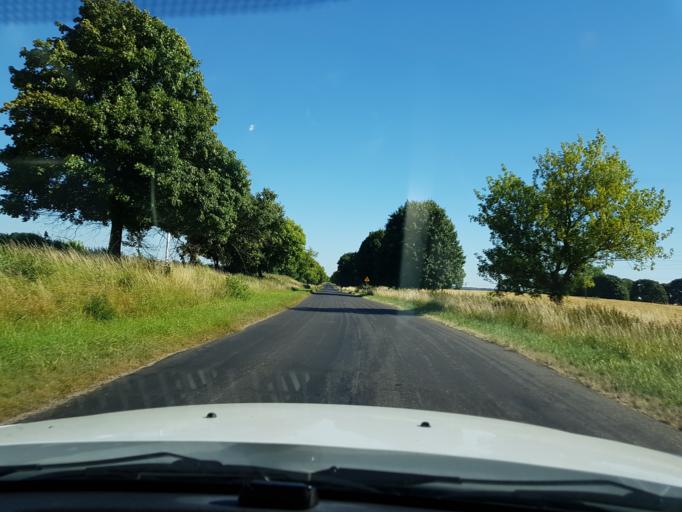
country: PL
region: West Pomeranian Voivodeship
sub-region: Powiat lobeski
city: Lobez
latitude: 53.6760
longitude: 15.6041
